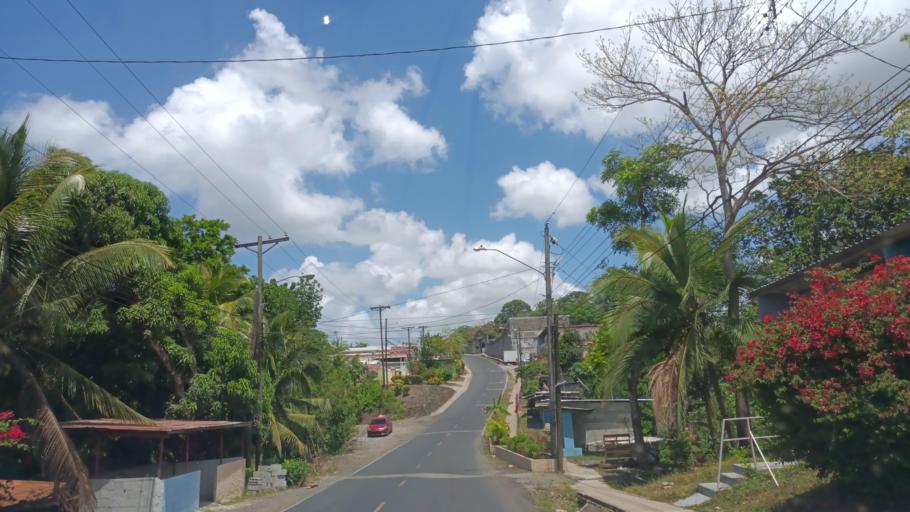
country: PA
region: Panama
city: Alcalde Diaz
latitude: 9.1073
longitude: -79.5626
